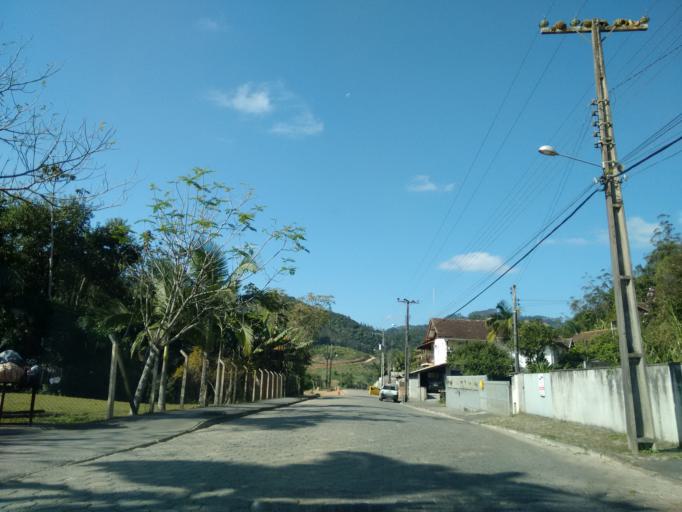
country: BR
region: Santa Catarina
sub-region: Pomerode
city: Pomerode
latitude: -26.7387
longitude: -49.1710
